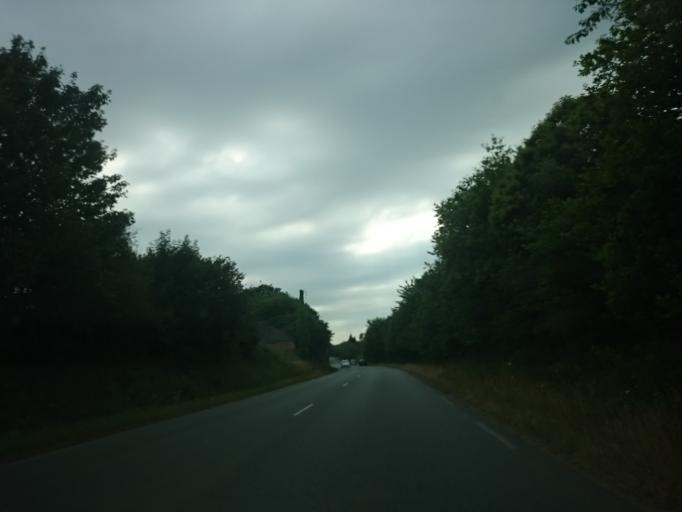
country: FR
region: Brittany
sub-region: Departement du Finistere
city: Saint-Renan
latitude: 48.4252
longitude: -4.6118
